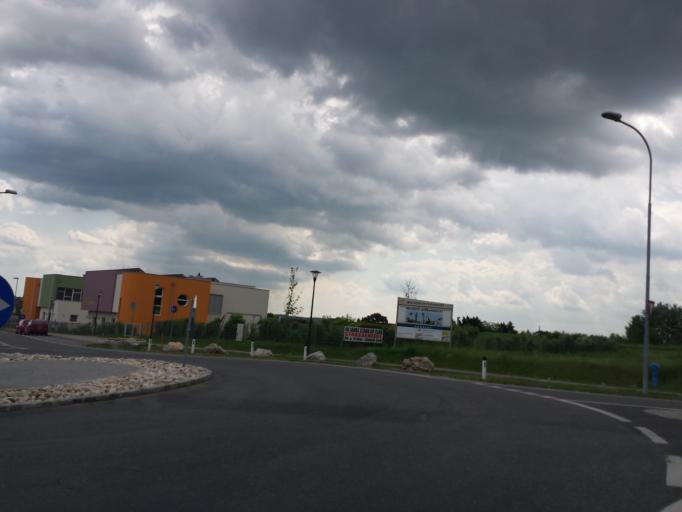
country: AT
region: Lower Austria
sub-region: Politischer Bezirk Wien-Umgebung
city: Fischamend Dorf
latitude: 48.1215
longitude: 16.5989
